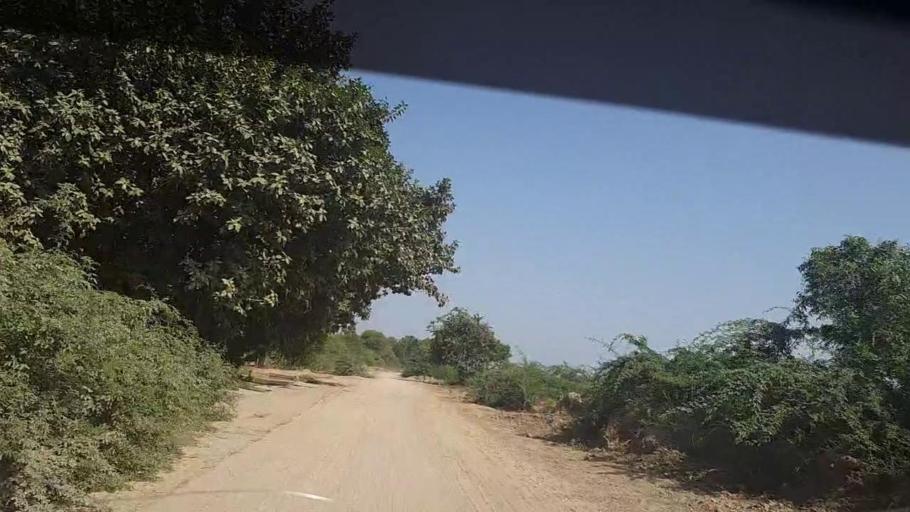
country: PK
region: Sindh
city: Rajo Khanani
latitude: 24.9695
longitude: 68.8756
